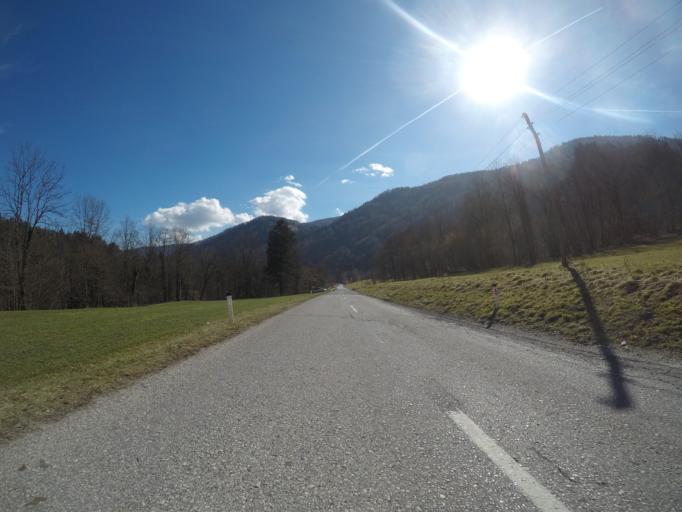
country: SI
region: Selnica ob Dravi
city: Selnica ob Dravi
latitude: 46.5384
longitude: 15.4530
